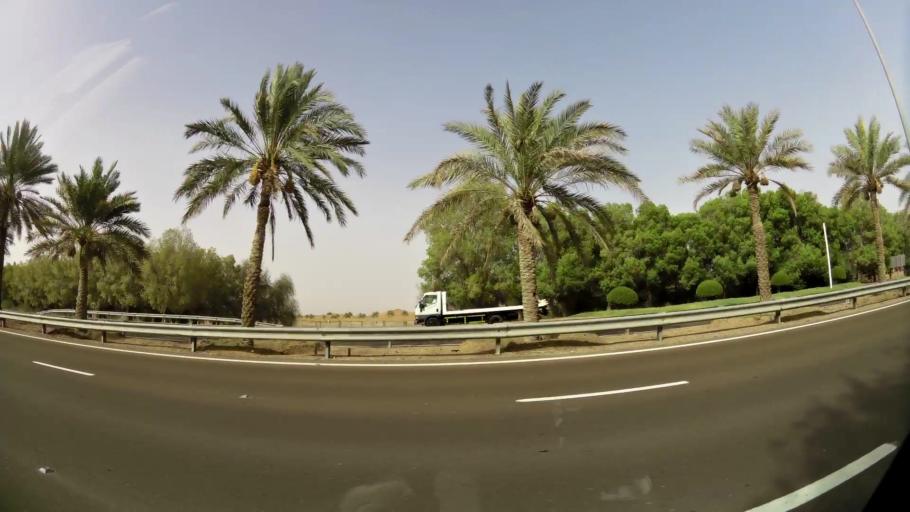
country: AE
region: Abu Dhabi
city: Al Ain
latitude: 24.1944
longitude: 55.5894
